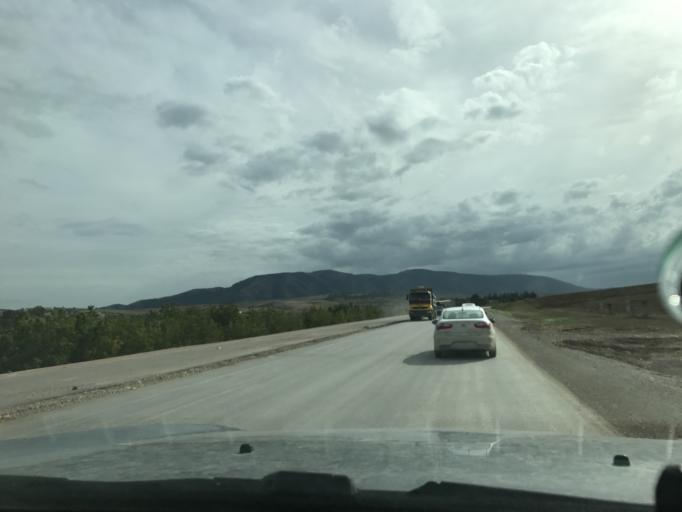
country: TN
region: Silyanah
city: Bu `Aradah
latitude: 36.1479
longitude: 9.6314
